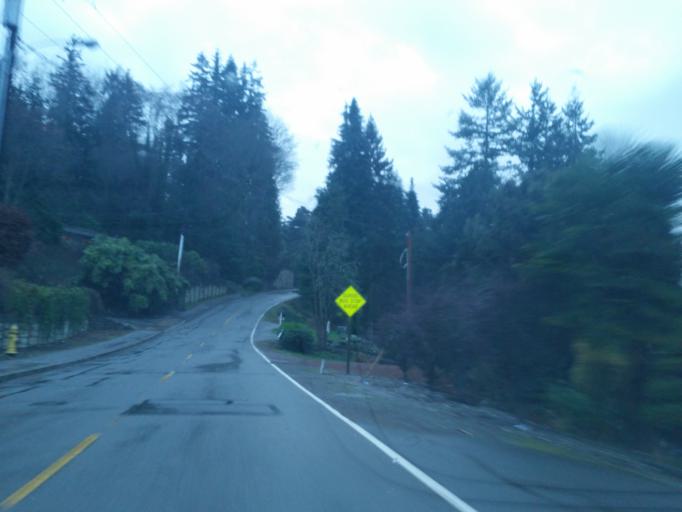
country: US
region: Washington
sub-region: Snohomish County
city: Meadowdale
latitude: 47.8506
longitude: -122.3352
